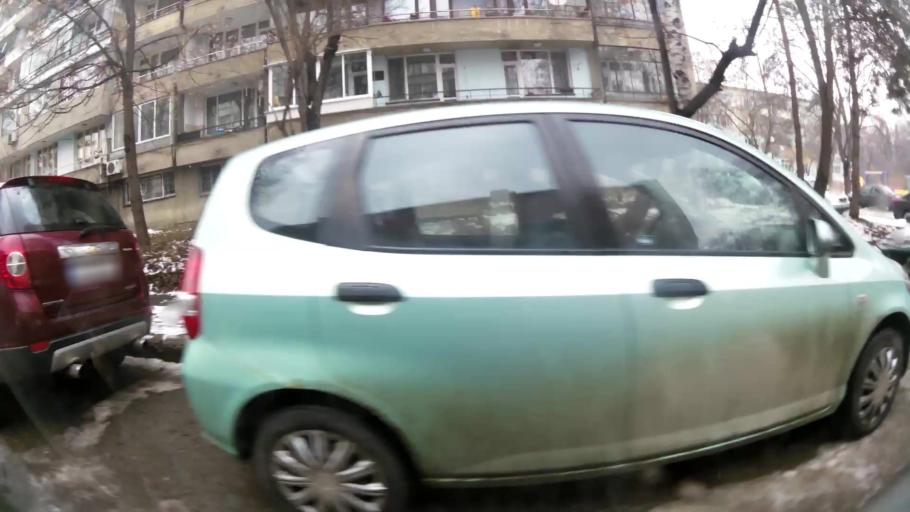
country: BG
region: Sofia-Capital
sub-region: Stolichna Obshtina
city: Sofia
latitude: 42.6805
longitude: 23.2927
